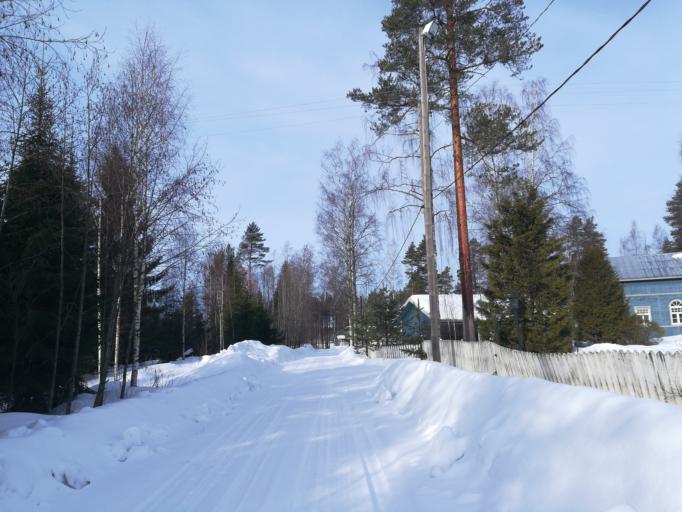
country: FI
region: Southern Savonia
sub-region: Savonlinna
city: Savonlinna
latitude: 61.8282
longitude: 29.0260
